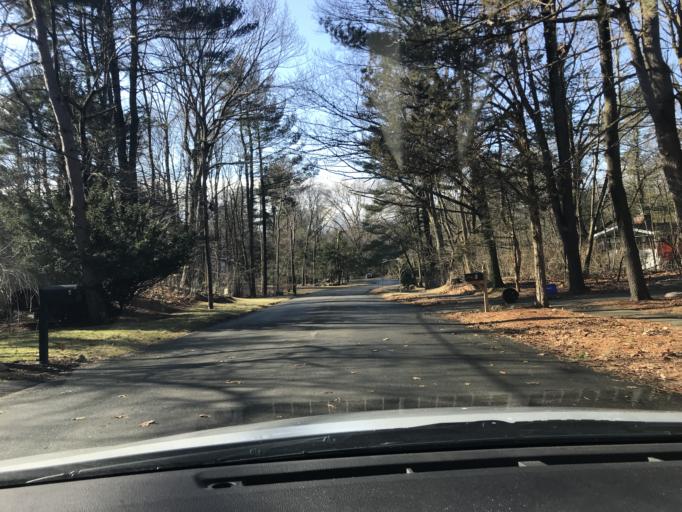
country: US
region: Massachusetts
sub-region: Middlesex County
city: Lexington
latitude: 42.4755
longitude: -71.2292
